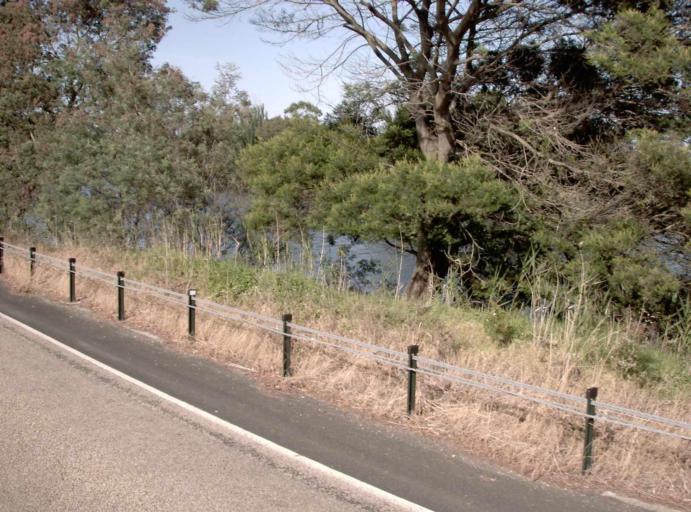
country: AU
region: Victoria
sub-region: East Gippsland
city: Lakes Entrance
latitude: -37.8396
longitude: 147.8601
